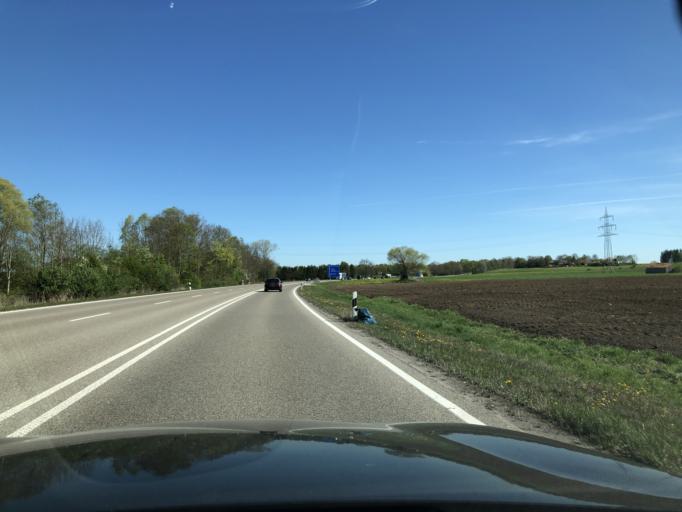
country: DE
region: Bavaria
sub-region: Swabia
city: Buchloe
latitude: 48.0202
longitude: 10.7231
